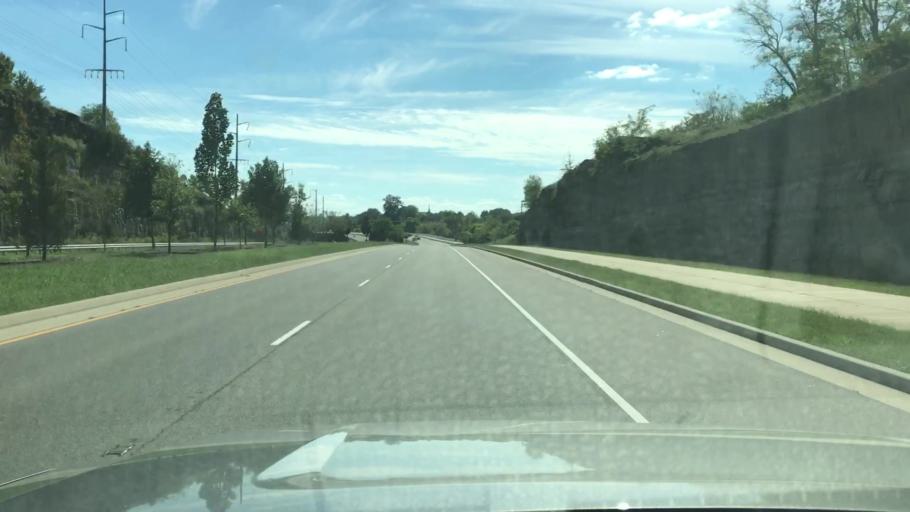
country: US
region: Tennessee
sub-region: Williamson County
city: Franklin
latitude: 35.9351
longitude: -86.8398
